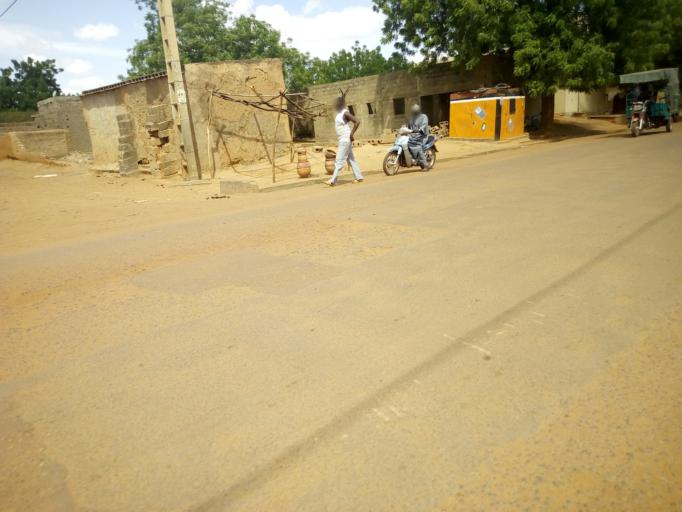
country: ML
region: Segou
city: Segou
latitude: 13.4323
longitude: -6.2635
